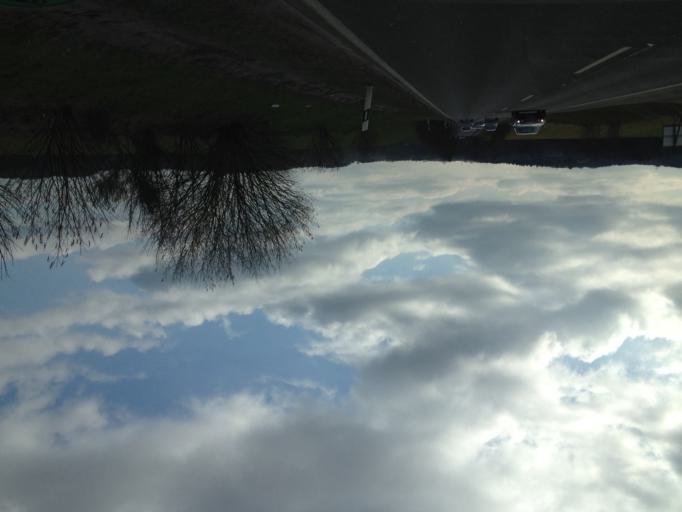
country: DE
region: Saarland
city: Oberthal
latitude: 49.4690
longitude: 7.1162
